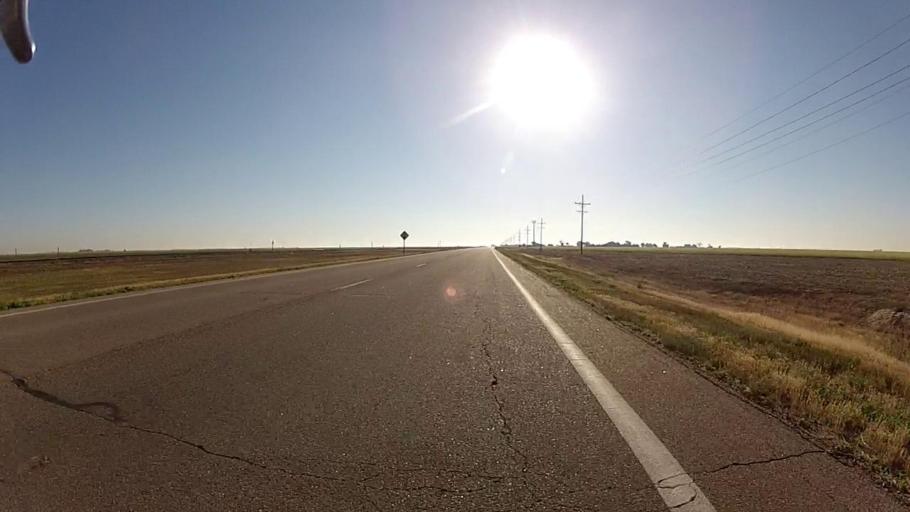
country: US
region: Kansas
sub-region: Haskell County
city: Sublette
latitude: 37.4885
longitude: -100.8254
